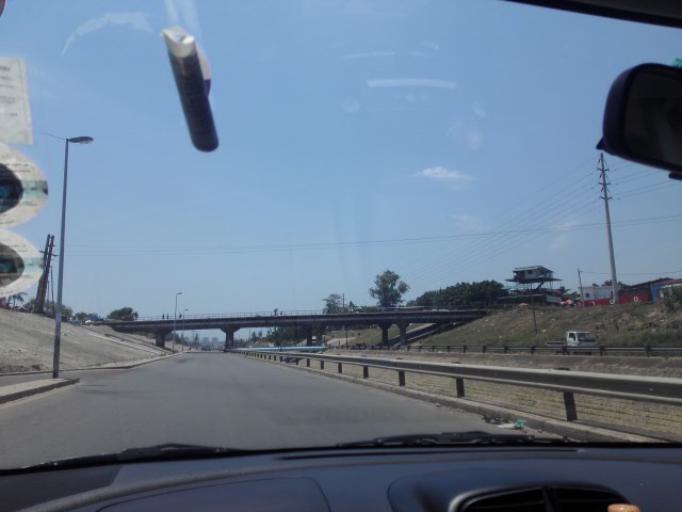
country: MZ
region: Maputo City
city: Maputo
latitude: -25.9328
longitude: 32.5612
